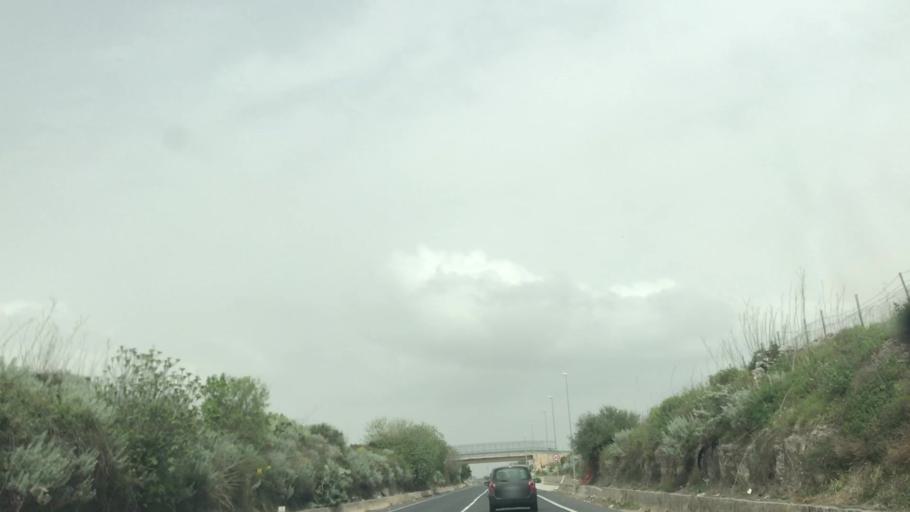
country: IT
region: Sicily
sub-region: Ragusa
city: Ragusa
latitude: 36.8766
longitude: 14.6936
